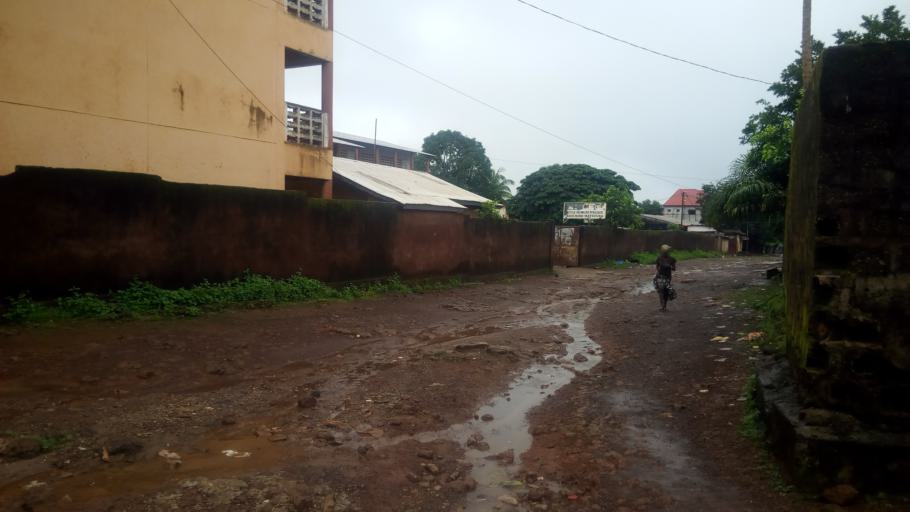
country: GN
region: Conakry
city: Conakry
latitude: 9.6375
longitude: -13.5604
